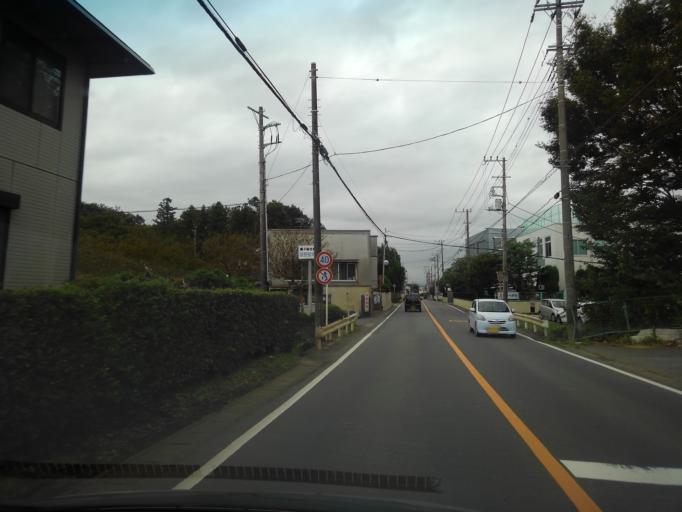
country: JP
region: Saitama
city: Sayama
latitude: 35.7904
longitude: 139.3910
